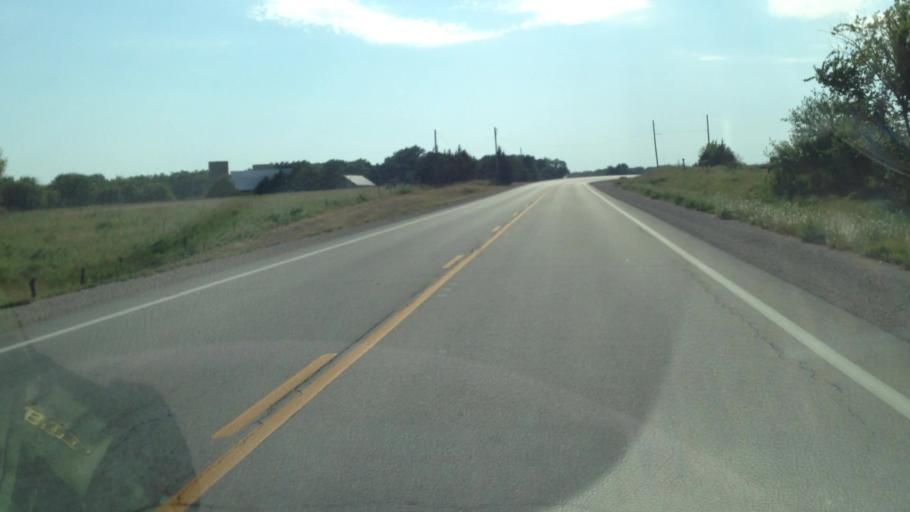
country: US
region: Kansas
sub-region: Anderson County
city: Garnett
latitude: 38.0817
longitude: -95.2359
